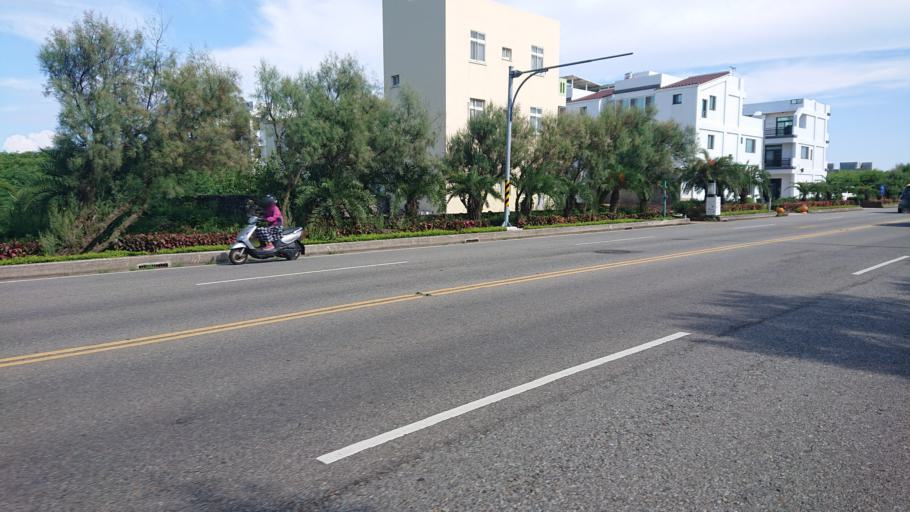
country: TW
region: Taiwan
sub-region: Penghu
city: Ma-kung
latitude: 23.5377
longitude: 119.6038
